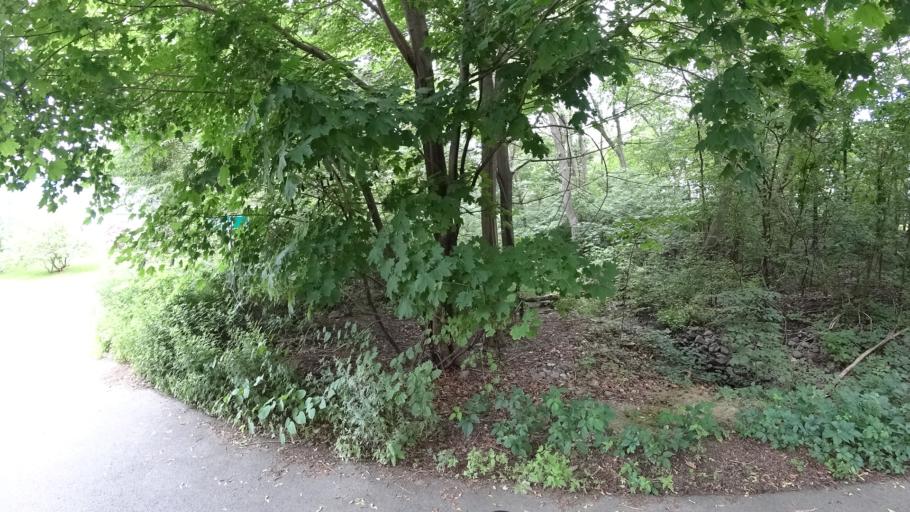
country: US
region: Massachusetts
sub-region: Norfolk County
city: Dedham
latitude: 42.2250
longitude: -71.1499
